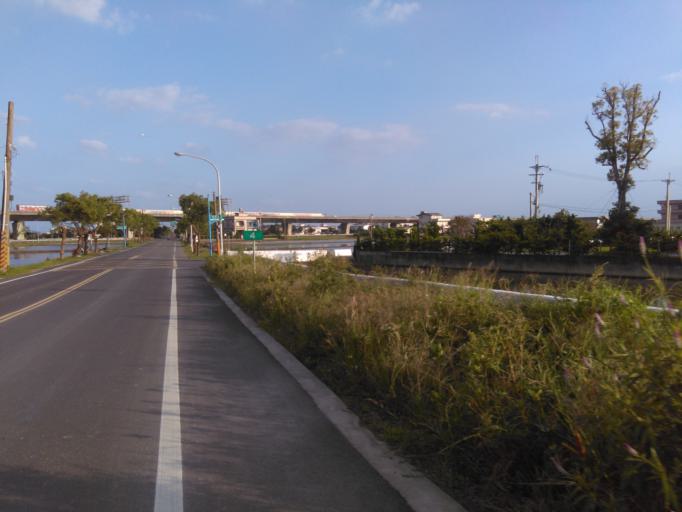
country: TW
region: Taiwan
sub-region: Yilan
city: Yilan
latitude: 24.8021
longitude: 121.7801
